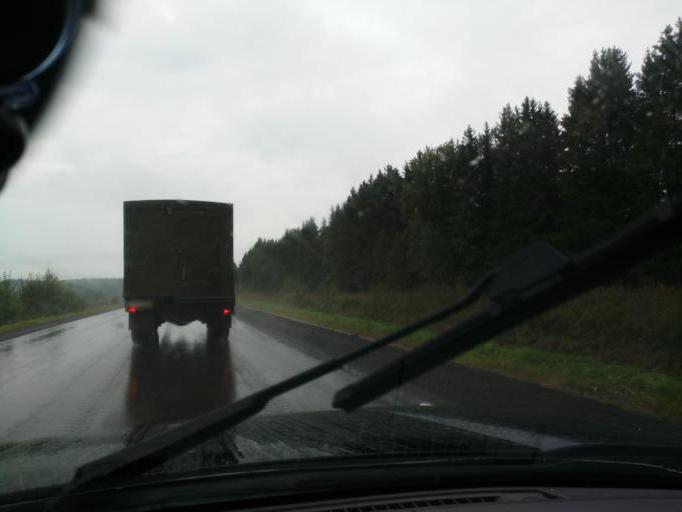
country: RU
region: Perm
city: Yugo-Kamskiy
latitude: 57.4726
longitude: 55.6772
